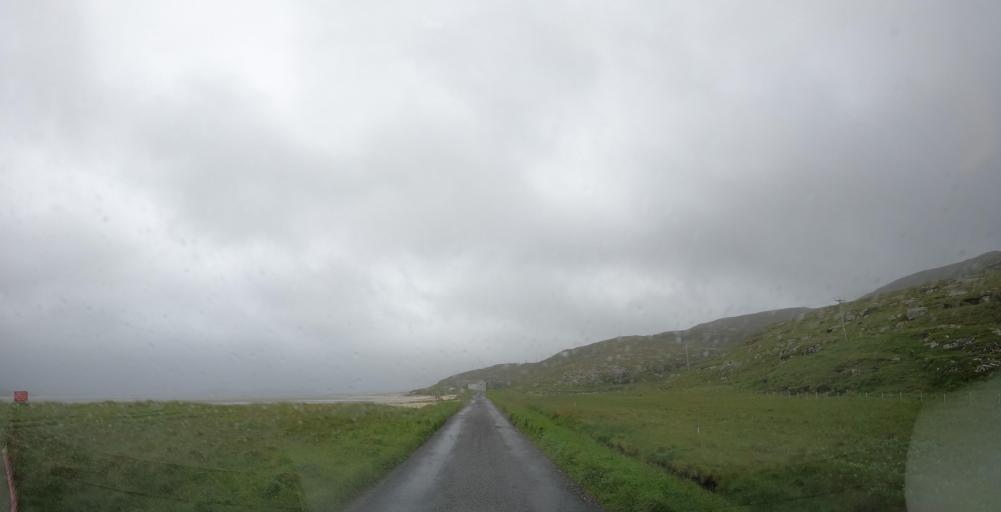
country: GB
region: Scotland
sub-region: Eilean Siar
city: Barra
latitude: 57.0201
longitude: -7.4469
